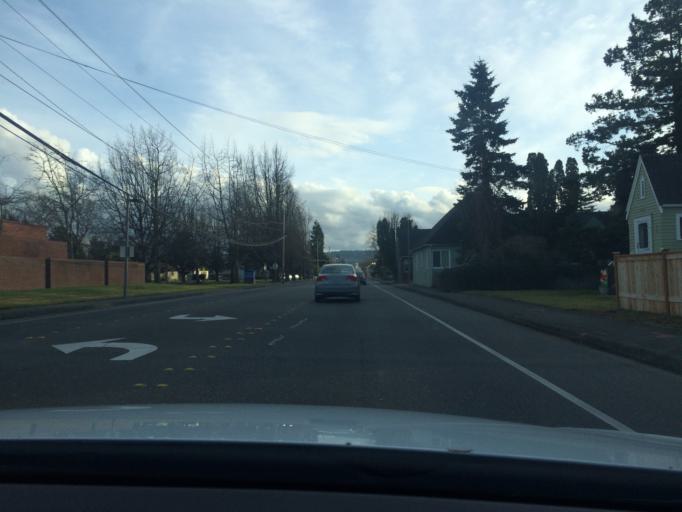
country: US
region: Washington
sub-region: Whatcom County
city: Bellingham
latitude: 48.7708
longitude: -122.4933
